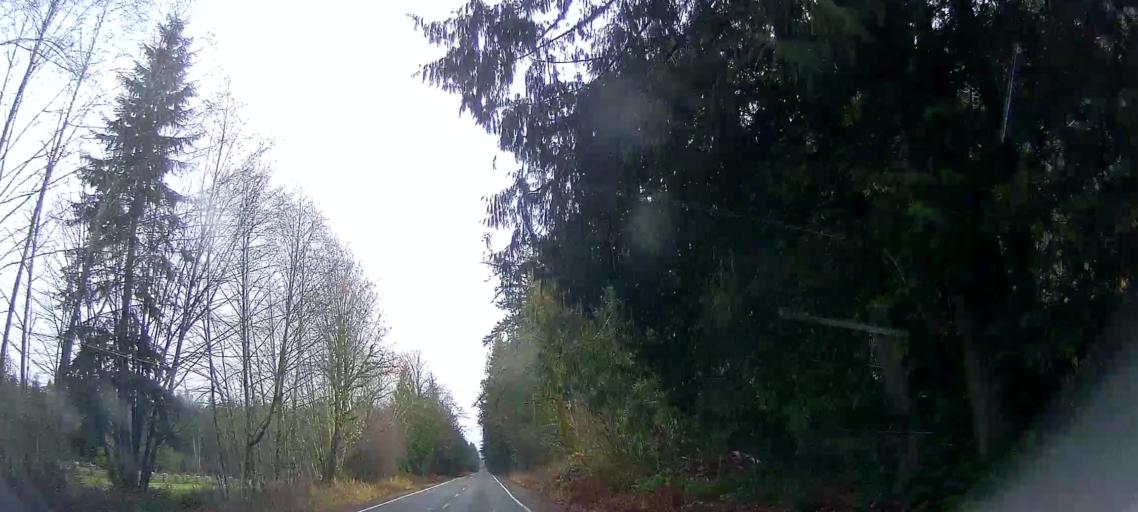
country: US
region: Washington
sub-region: Snohomish County
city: Darrington
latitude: 48.5307
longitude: -121.8116
